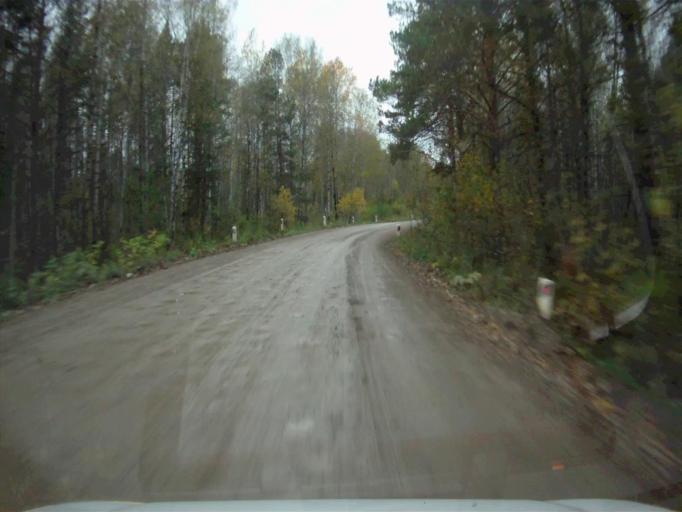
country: RU
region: Chelyabinsk
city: Nyazepetrovsk
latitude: 56.1269
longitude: 59.3356
